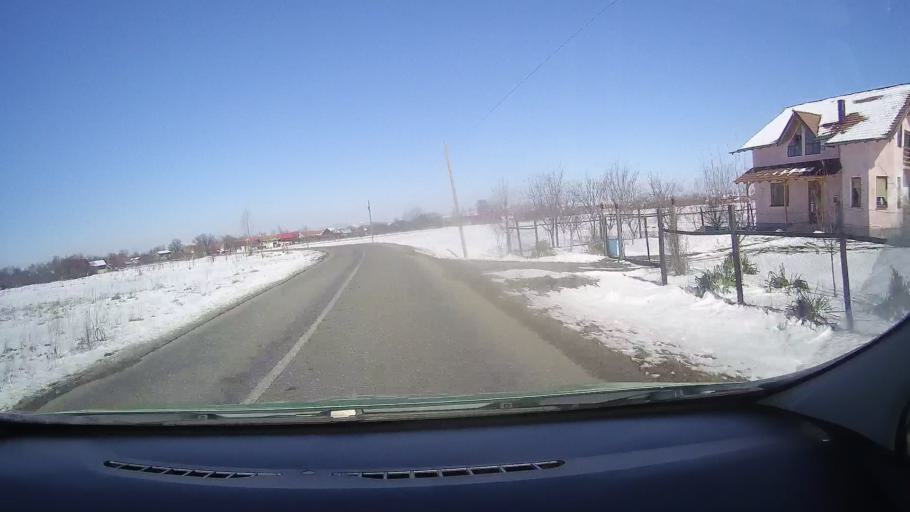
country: RO
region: Brasov
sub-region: Comuna Harseni
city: Harseni
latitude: 45.7831
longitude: 25.0014
